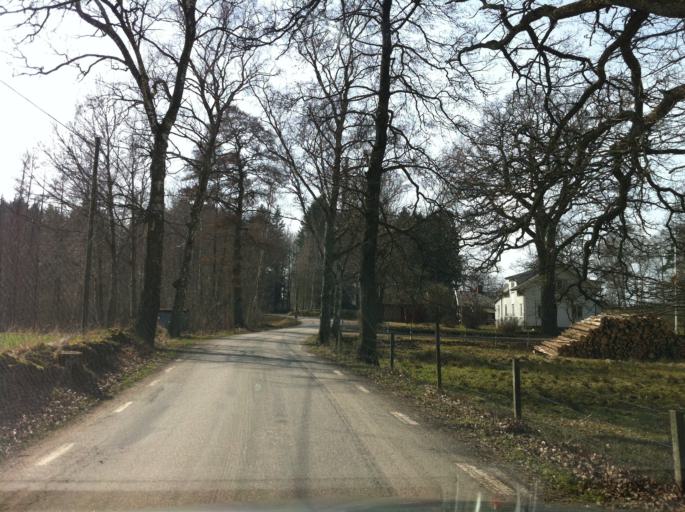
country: SE
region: Vaestra Goetaland
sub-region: Falkopings Kommun
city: Falkoeping
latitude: 58.2386
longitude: 13.5081
